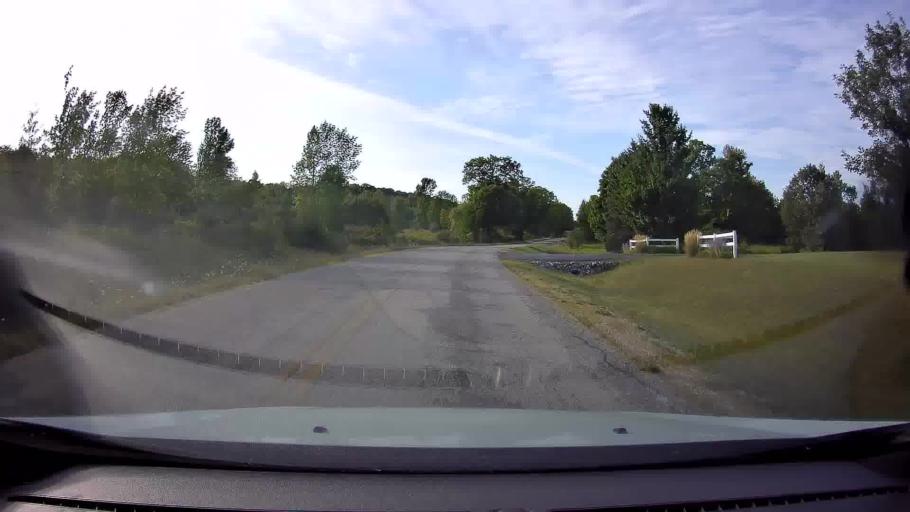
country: US
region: Wisconsin
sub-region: Door County
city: Sturgeon Bay
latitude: 45.1770
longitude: -87.1432
